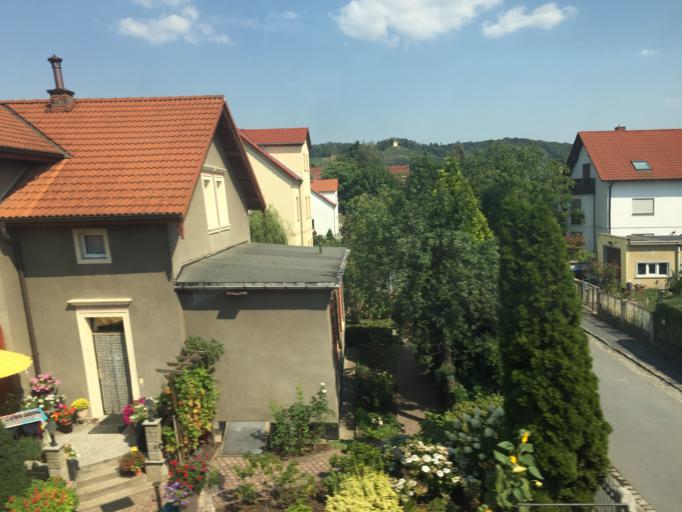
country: DE
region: Saxony
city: Radebeul
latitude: 51.1060
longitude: 13.6370
